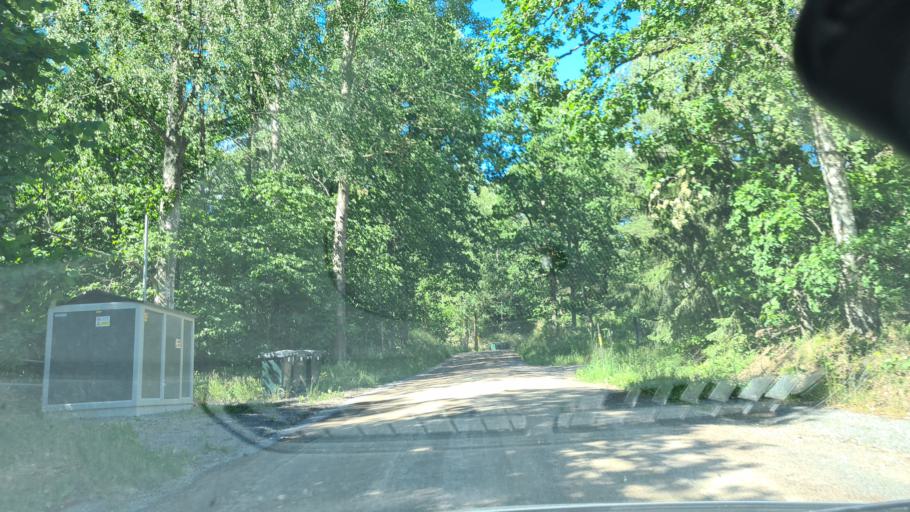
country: SE
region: OEstergoetland
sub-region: Norrkopings Kommun
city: Krokek
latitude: 58.6733
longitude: 16.4225
